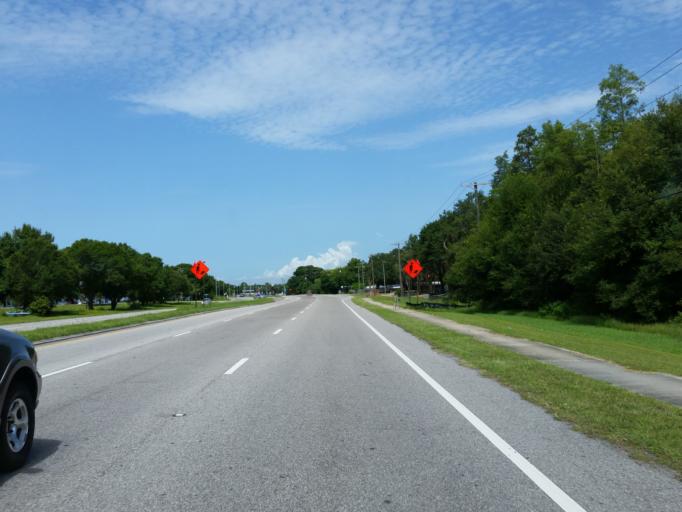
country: US
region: Florida
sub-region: Hillsborough County
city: Progress Village
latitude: 27.9231
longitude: -82.3423
